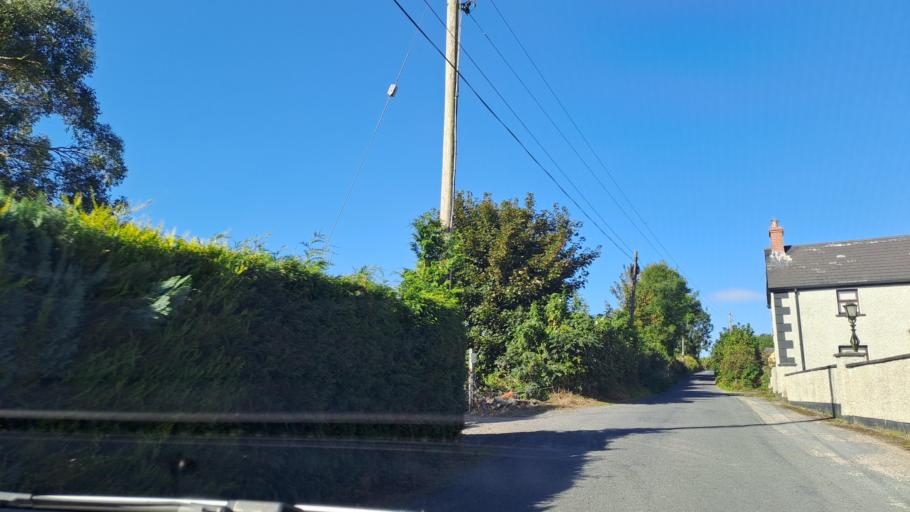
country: IE
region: Ulster
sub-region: County Monaghan
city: Carrickmacross
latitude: 53.9996
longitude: -6.7731
